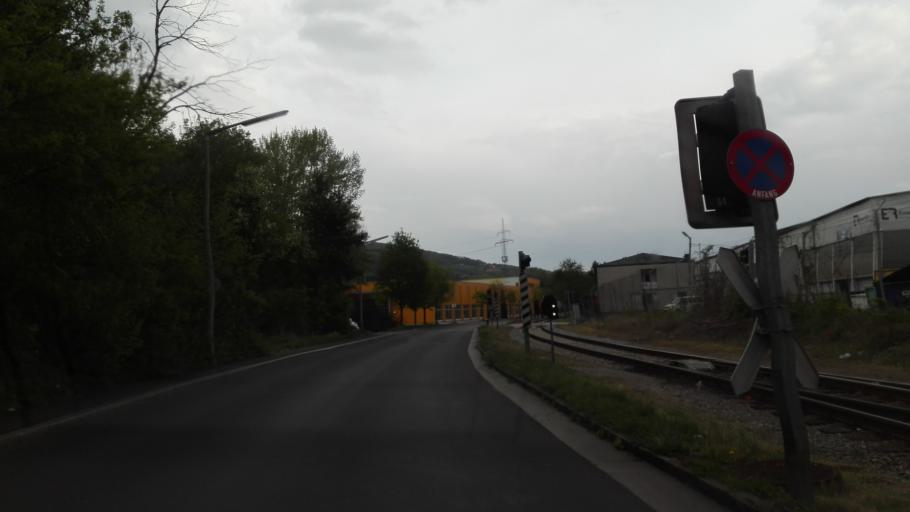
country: AT
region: Upper Austria
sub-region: Linz Stadt
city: Linz
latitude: 48.3103
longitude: 14.3266
